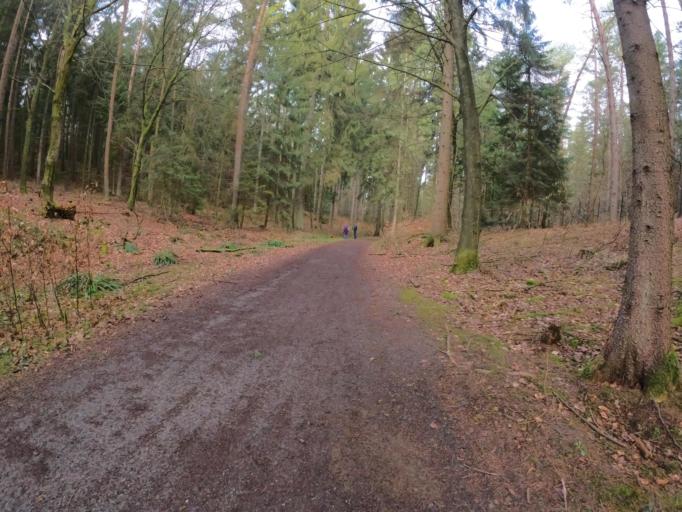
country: DE
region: Lower Saxony
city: Neu Wulmstorf
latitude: 53.4430
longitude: 9.8789
